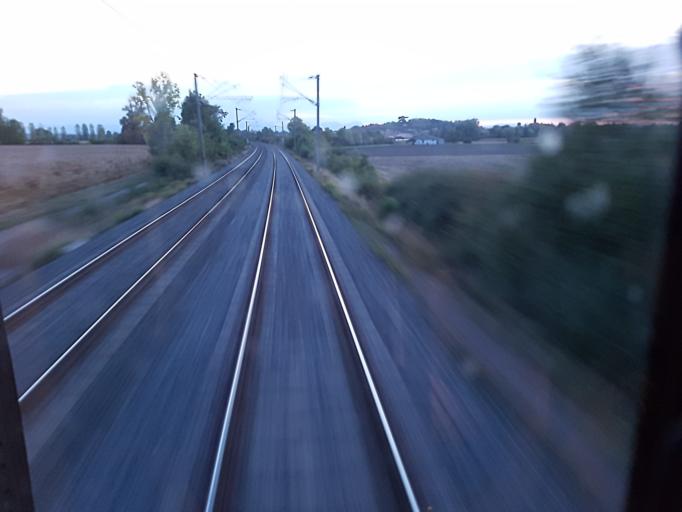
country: FR
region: Auvergne
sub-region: Departement du Puy-de-Dome
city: Maringues
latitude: 45.9722
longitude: 3.2709
